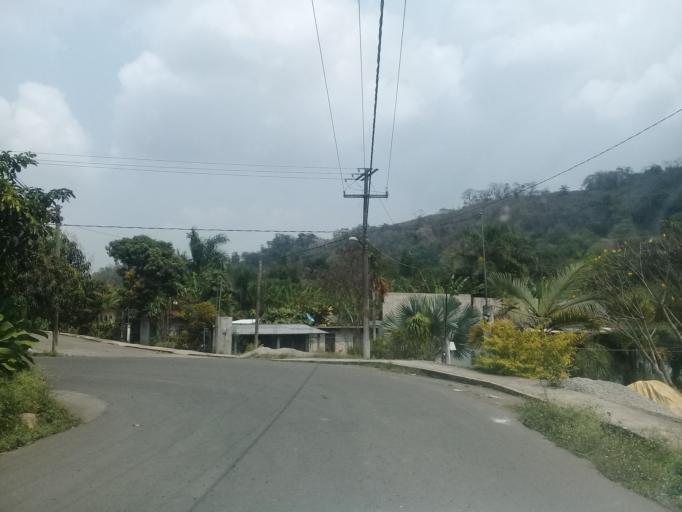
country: MX
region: Veracruz
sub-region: Cordoba
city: San Jose de Tapia
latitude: 18.8254
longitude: -96.9790
